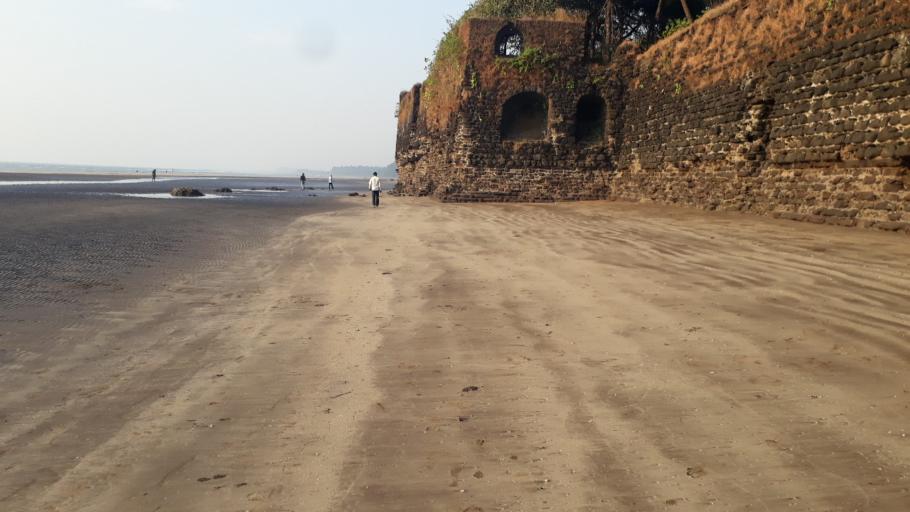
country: IN
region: Maharashtra
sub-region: Raigarh
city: Revadanda
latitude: 18.5469
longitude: 72.9241
